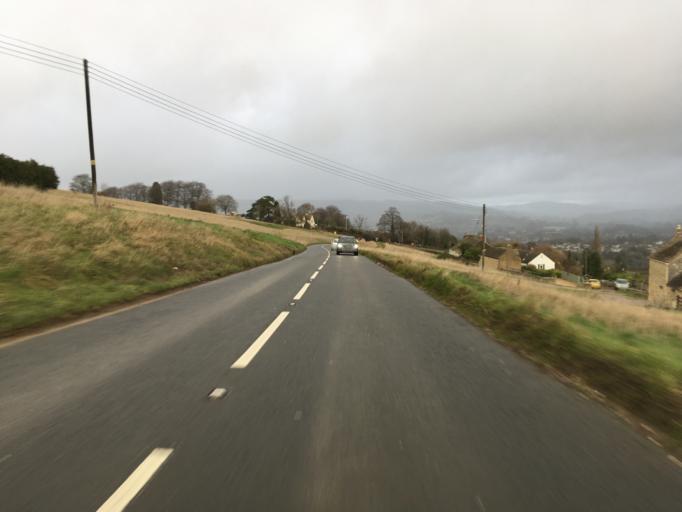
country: GB
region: England
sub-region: Gloucestershire
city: Nailsworth
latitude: 51.7287
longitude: -2.2432
